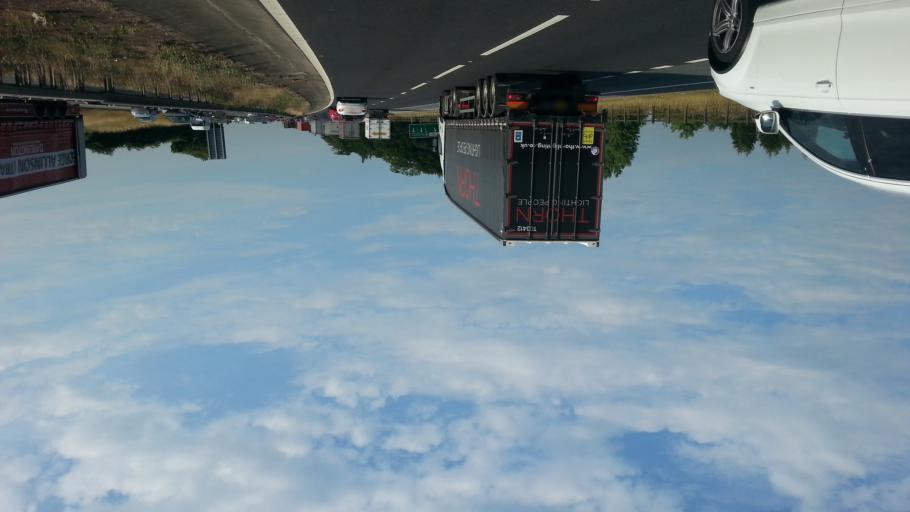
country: GB
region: England
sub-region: City and Borough of Wakefield
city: Darrington
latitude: 53.6814
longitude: -1.2626
